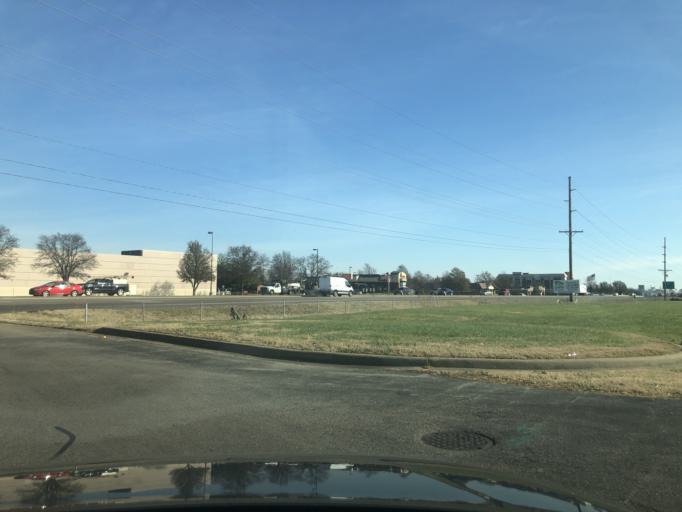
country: US
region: Indiana
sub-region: Vanderburgh County
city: Melody Hill
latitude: 37.9763
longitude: -87.4692
